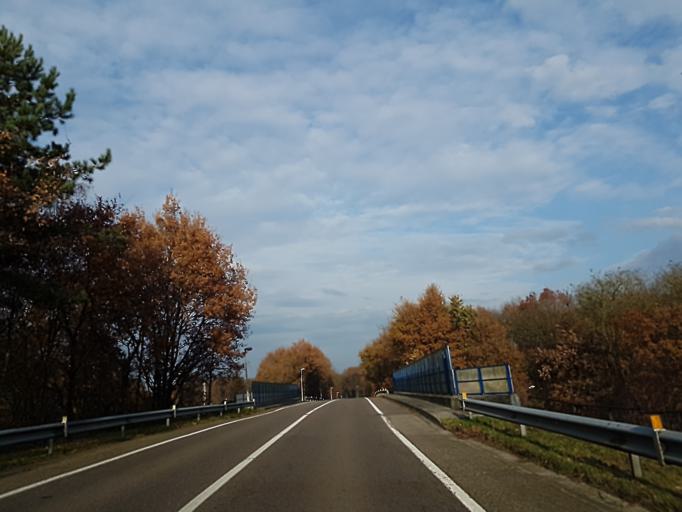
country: BE
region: Flanders
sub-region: Provincie Antwerpen
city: Essen
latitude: 51.4329
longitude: 4.4613
